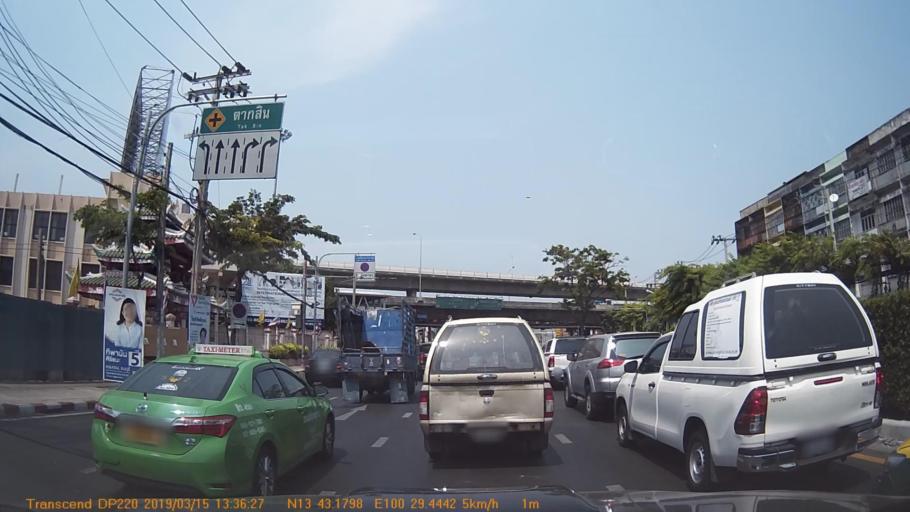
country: TH
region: Bangkok
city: Thon Buri
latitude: 13.7197
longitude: 100.4907
